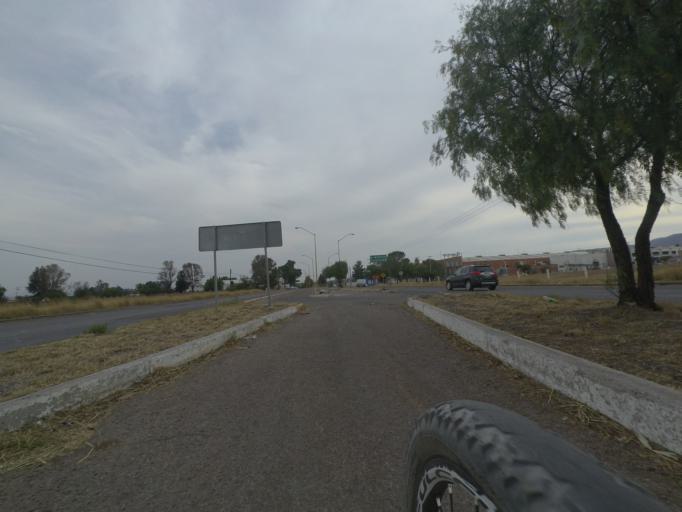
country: MX
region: Aguascalientes
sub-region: Aguascalientes
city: La Loma de los Negritos
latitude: 21.8678
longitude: -102.3712
